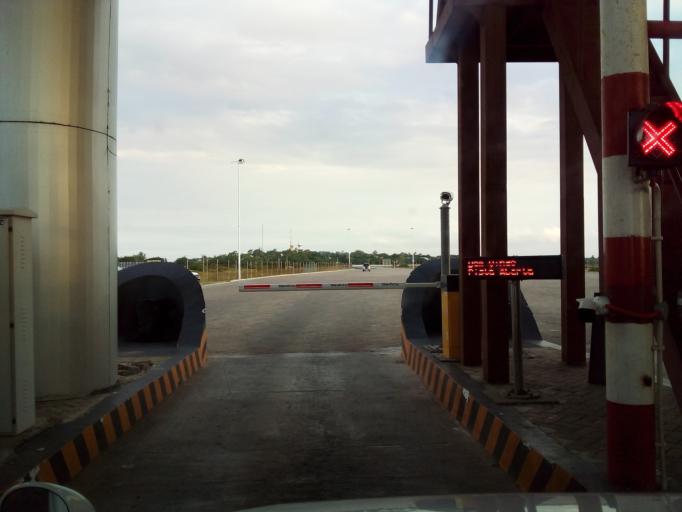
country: MZ
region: Maputo City
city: Maputo
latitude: -25.9959
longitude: 32.5561
